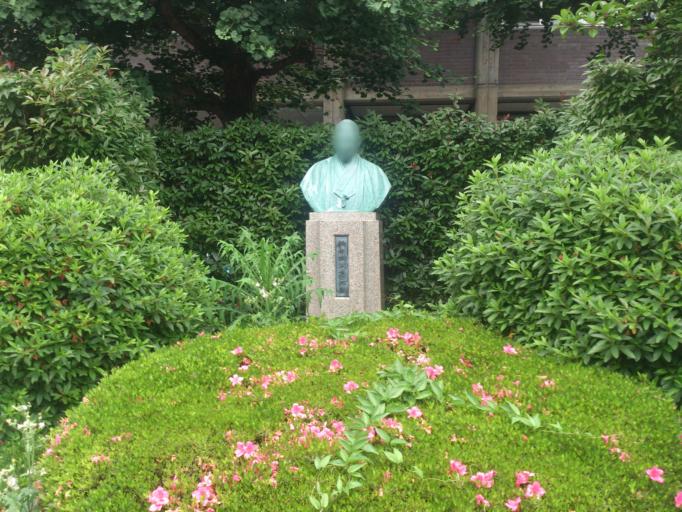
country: JP
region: Ehime
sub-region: Shikoku-chuo Shi
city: Matsuyama
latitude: 33.8509
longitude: 132.7695
